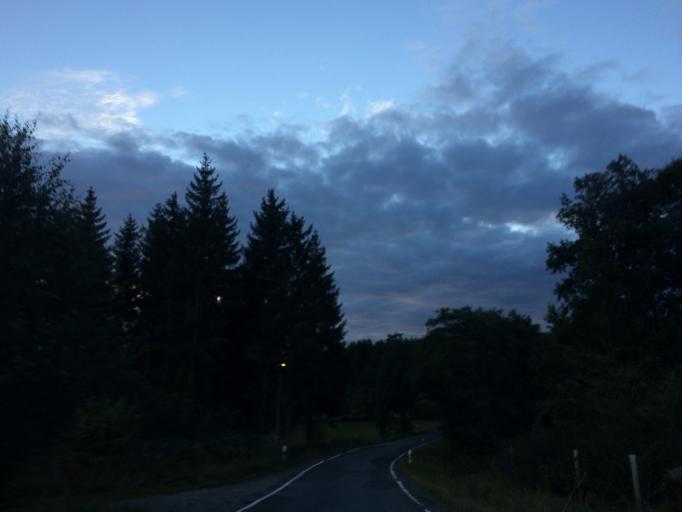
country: DE
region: Thuringia
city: Keila
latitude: 50.6473
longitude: 11.6743
